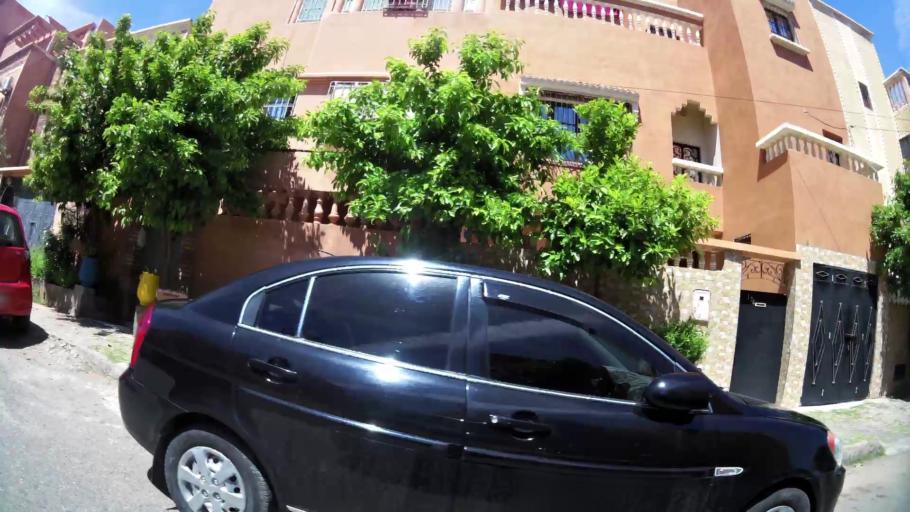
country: MA
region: Marrakech-Tensift-Al Haouz
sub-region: Marrakech
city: Marrakesh
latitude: 31.6423
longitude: -8.0541
